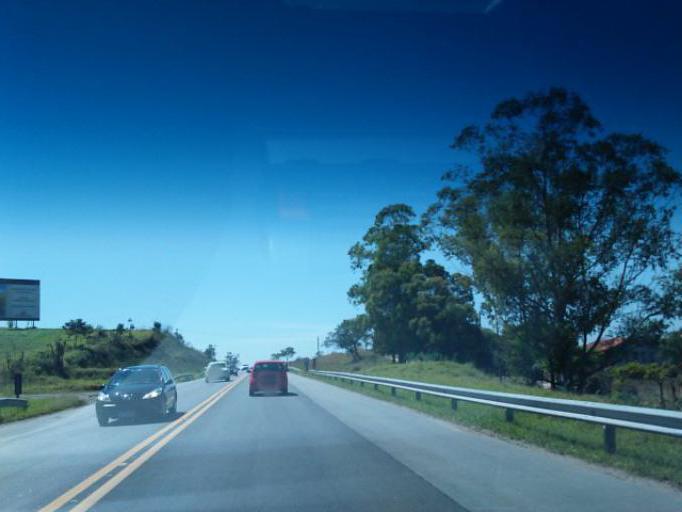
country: BR
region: Sao Paulo
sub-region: Tremembe
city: Tremembe
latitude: -22.9600
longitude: -45.6316
